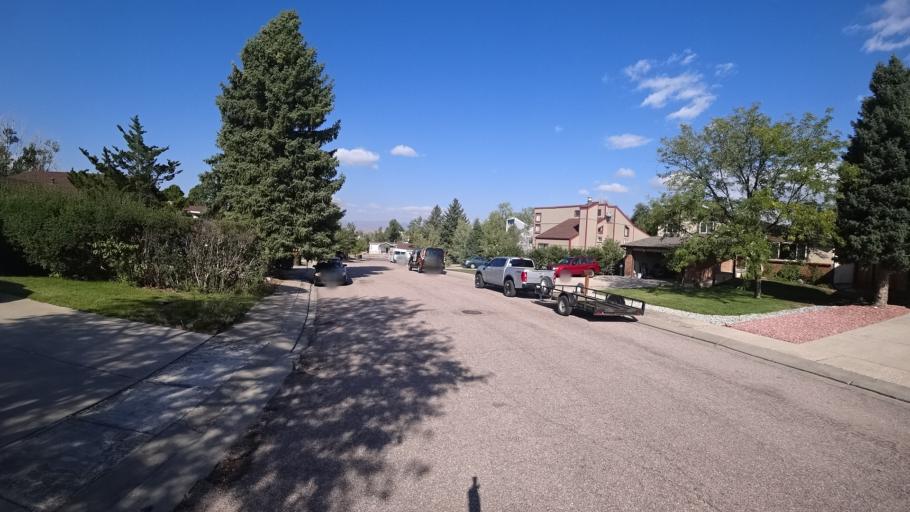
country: US
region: Colorado
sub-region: El Paso County
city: Cimarron Hills
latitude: 38.8839
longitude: -104.7287
